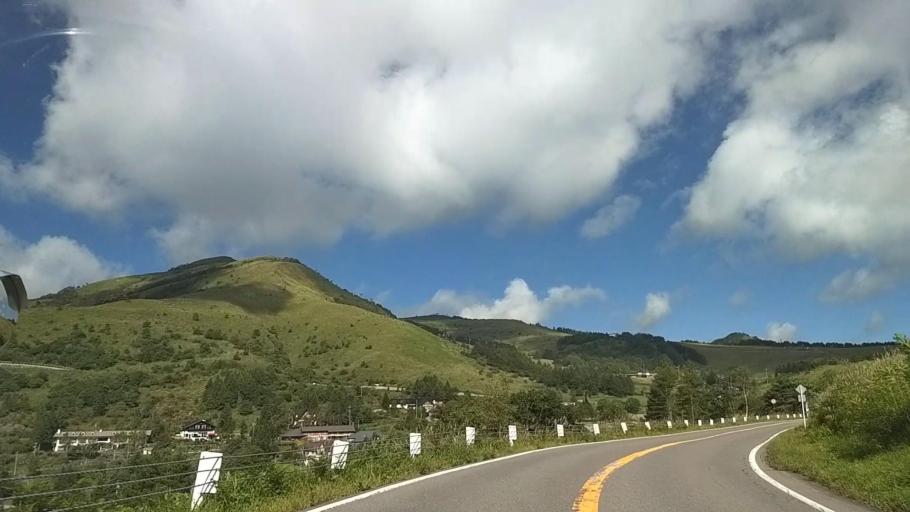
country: JP
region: Nagano
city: Suwa
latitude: 36.0967
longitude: 138.2159
